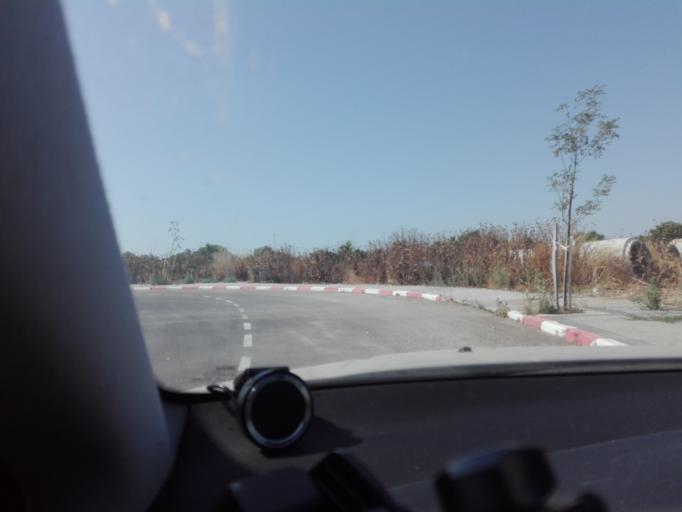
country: IL
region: Central District
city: Bene 'Ayish
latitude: 31.7289
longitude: 34.7584
